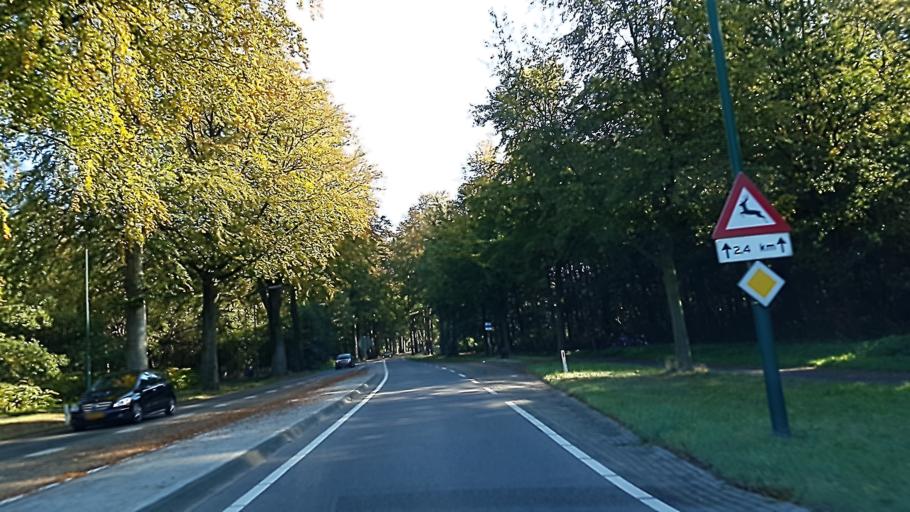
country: BE
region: Flanders
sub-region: Provincie Antwerpen
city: Stabroek
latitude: 51.3828
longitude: 4.3729
